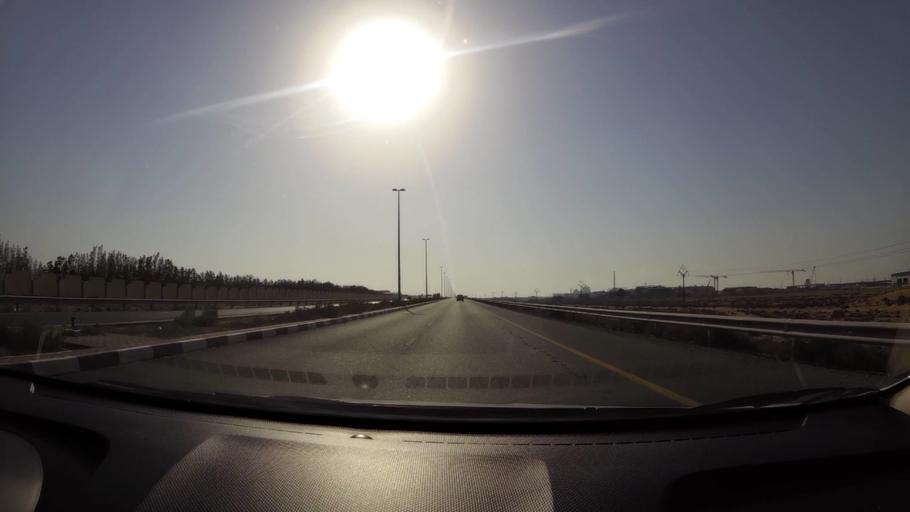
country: AE
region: Umm al Qaywayn
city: Umm al Qaywayn
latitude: 25.4333
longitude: 55.5728
